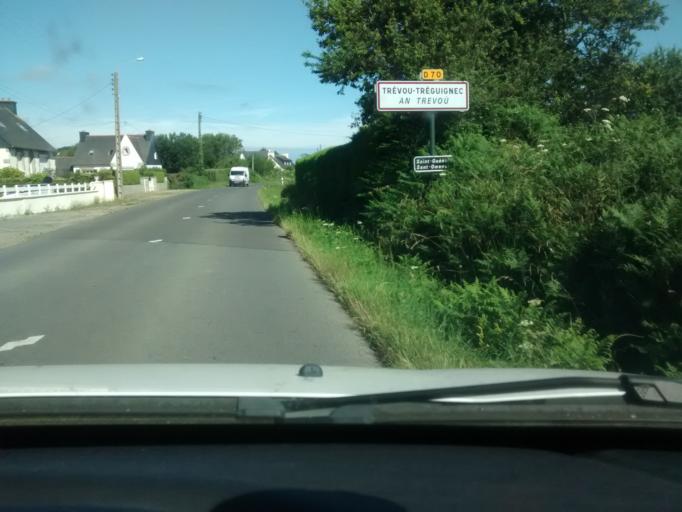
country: FR
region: Brittany
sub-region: Departement des Cotes-d'Armor
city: Trevou-Treguignec
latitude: 48.8095
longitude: -3.3300
